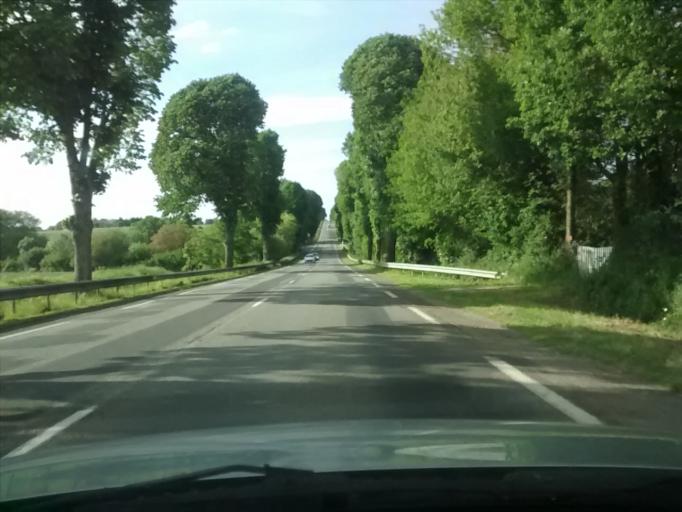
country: FR
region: Pays de la Loire
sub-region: Departement de la Mayenne
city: Chateau-Gontier
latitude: 47.8973
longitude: -0.6826
